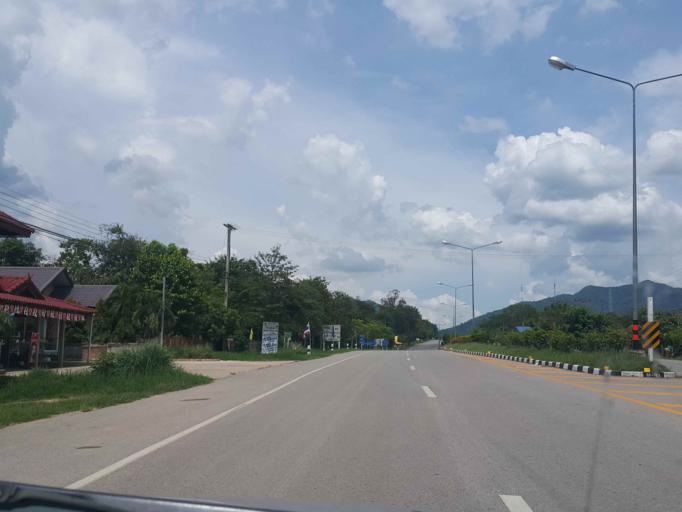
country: TH
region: Nan
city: Ban Luang
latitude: 18.8501
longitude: 100.4338
